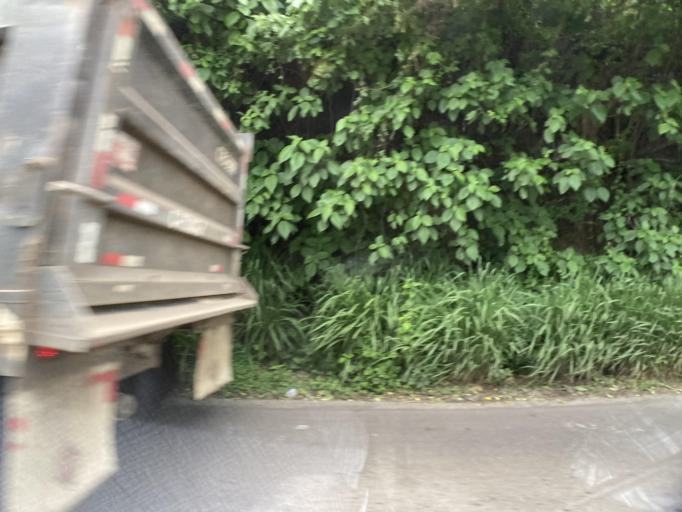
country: GT
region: Guatemala
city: Villa Canales
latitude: 14.4416
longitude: -90.5337
